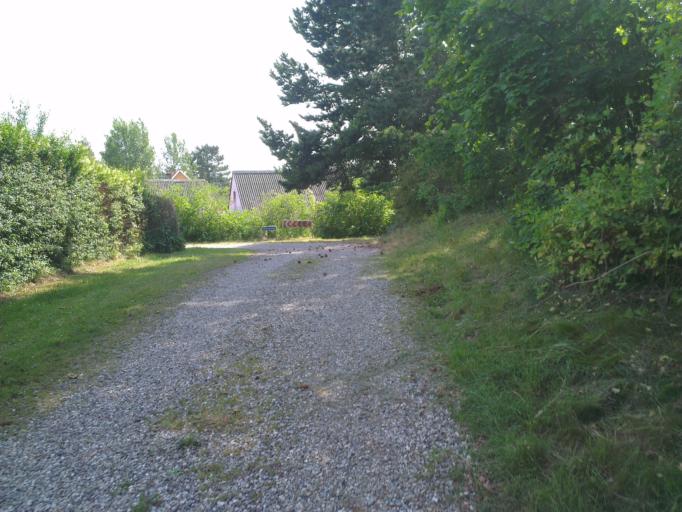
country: DK
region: Capital Region
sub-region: Halsnaes Kommune
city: Hundested
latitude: 55.9287
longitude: 11.9206
